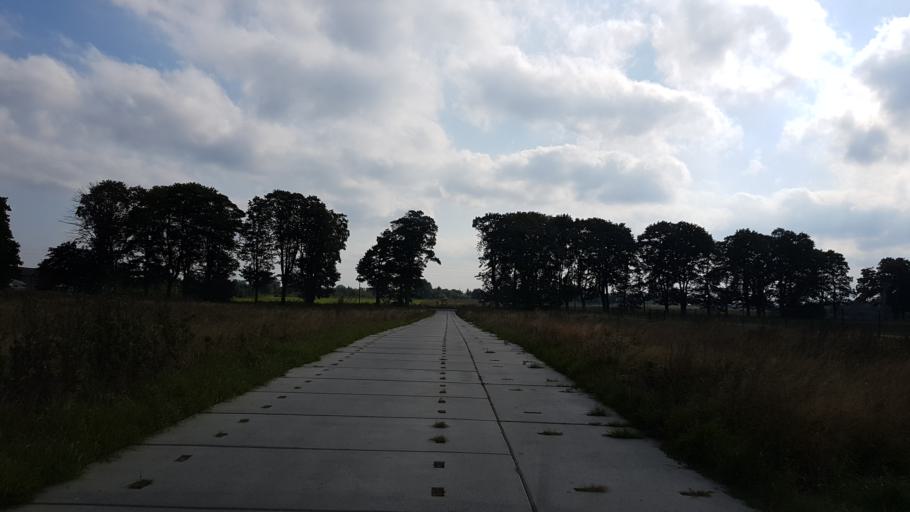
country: PL
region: West Pomeranian Voivodeship
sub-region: Koszalin
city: Koszalin
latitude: 54.1751
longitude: 16.1591
